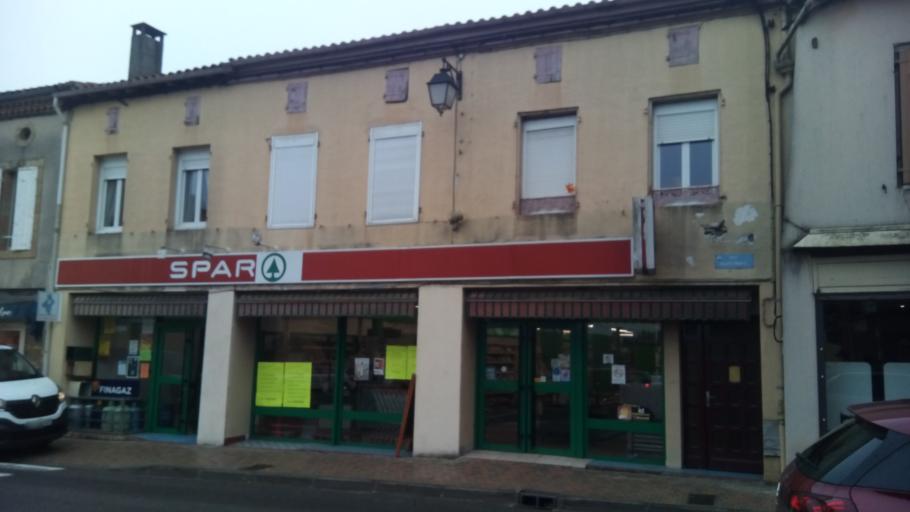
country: FR
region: Midi-Pyrenees
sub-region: Departement du Gers
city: Nogaro
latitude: 43.7589
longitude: -0.0332
